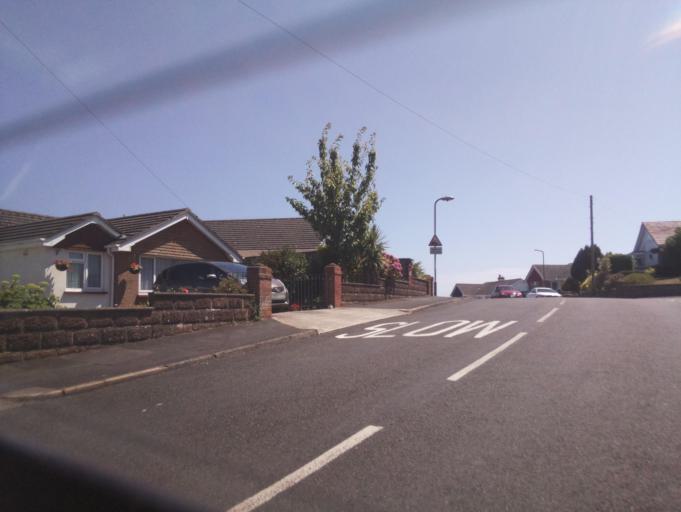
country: GB
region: England
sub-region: Borough of Torbay
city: Paignton
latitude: 50.4261
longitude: -3.5744
